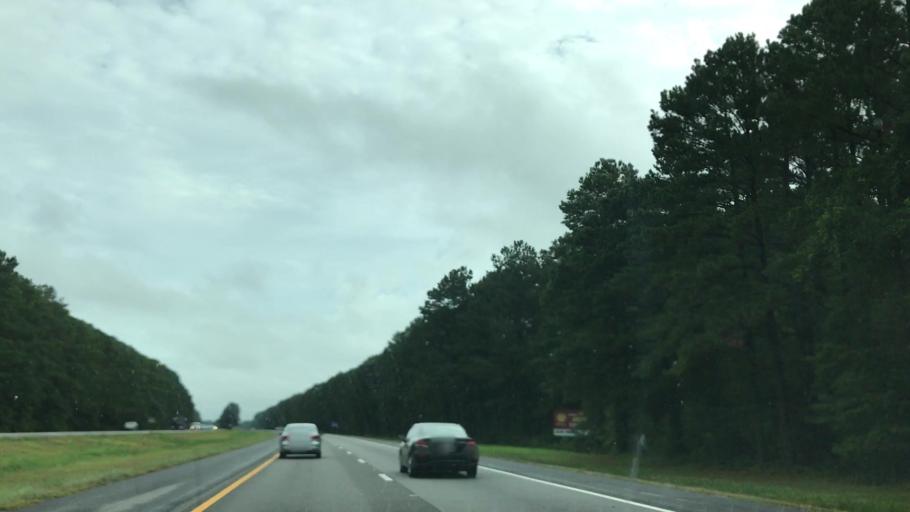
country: US
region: North Carolina
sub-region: Nash County
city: Red Oak
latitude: 36.0865
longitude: -77.8080
